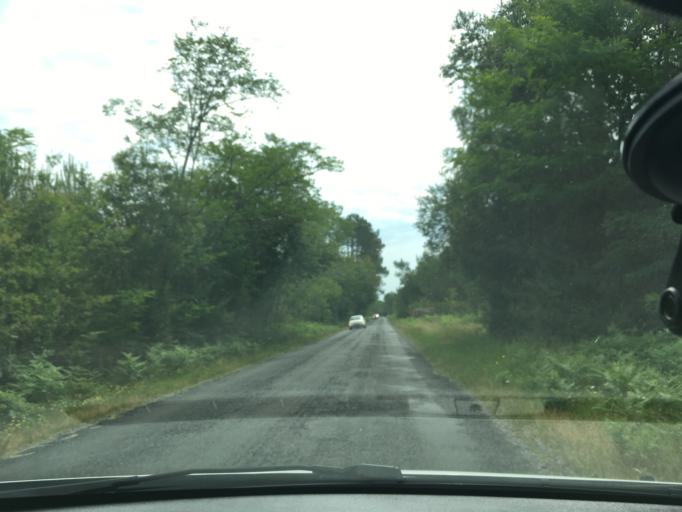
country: FR
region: Aquitaine
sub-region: Departement de la Gironde
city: Gaillan-en-Medoc
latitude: 45.3468
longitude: -1.0332
